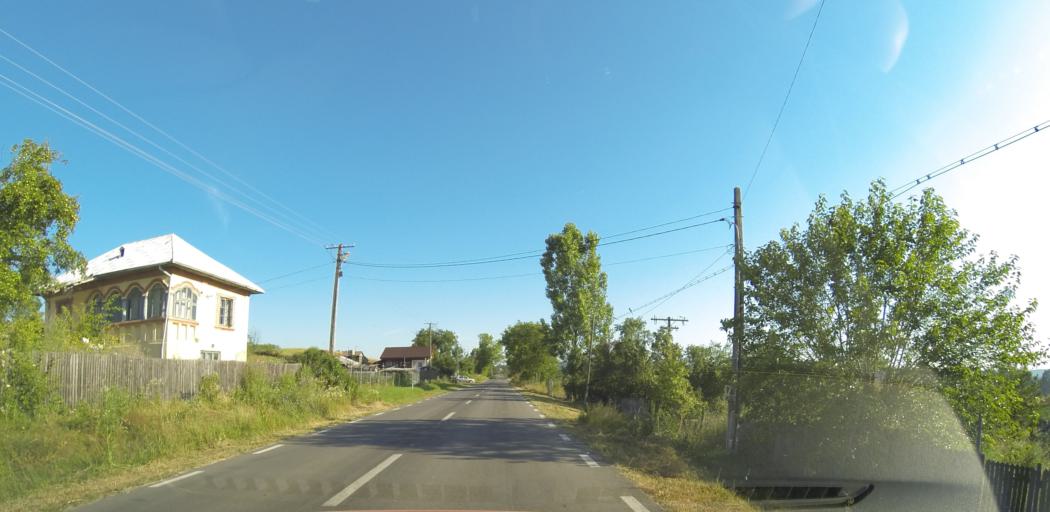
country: RO
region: Valcea
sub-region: Comuna Tetoiu
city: Tetoiu
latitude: 44.7260
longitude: 23.8981
